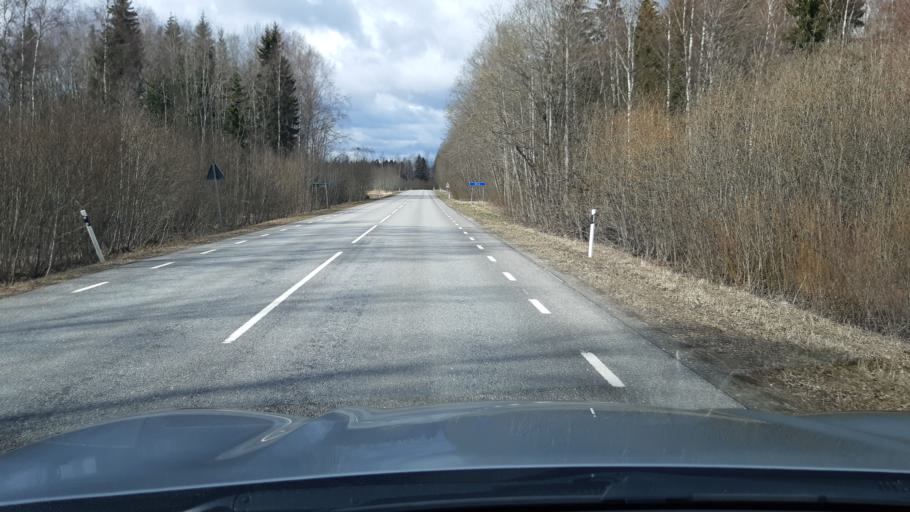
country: EE
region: Raplamaa
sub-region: Kehtna vald
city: Kehtna
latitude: 59.0436
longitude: 25.0295
